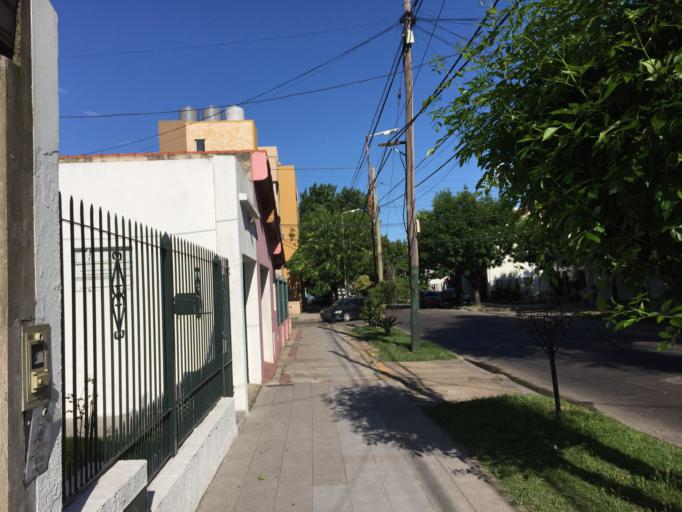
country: AR
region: Buenos Aires
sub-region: Partido de Lomas de Zamora
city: Lomas de Zamora
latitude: -34.7449
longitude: -58.3894
